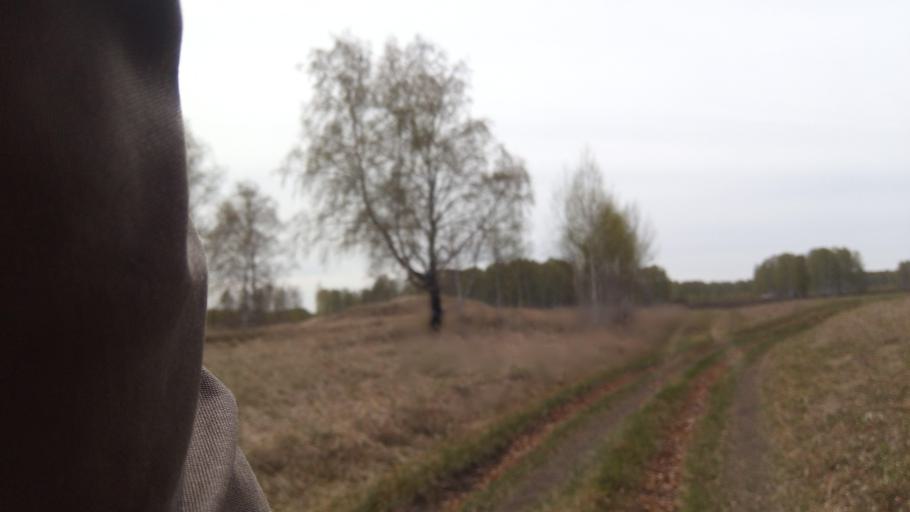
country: RU
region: Chelyabinsk
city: Timiryazevskiy
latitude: 55.0120
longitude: 60.8591
